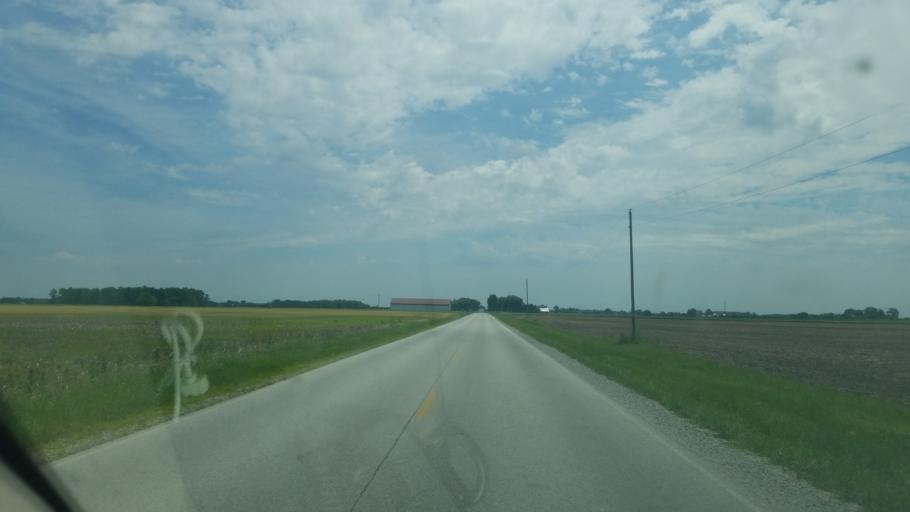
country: US
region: Ohio
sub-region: Wood County
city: Bowling Green
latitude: 41.2967
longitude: -83.6163
